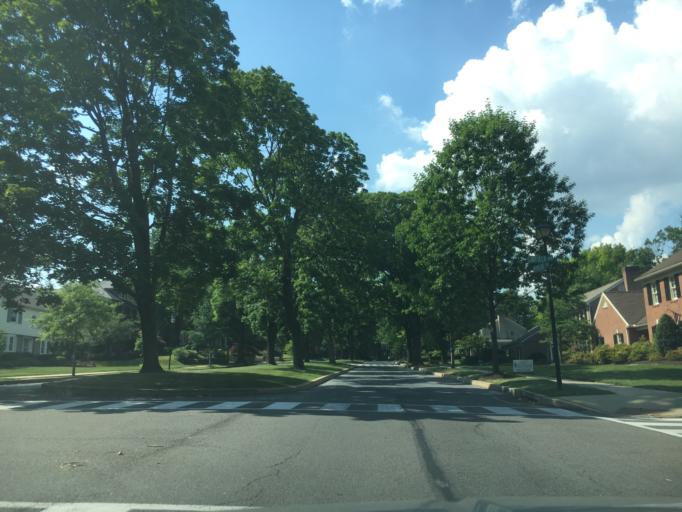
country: US
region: Pennsylvania
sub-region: Berks County
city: Wyomissing
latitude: 40.3299
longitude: -75.9635
